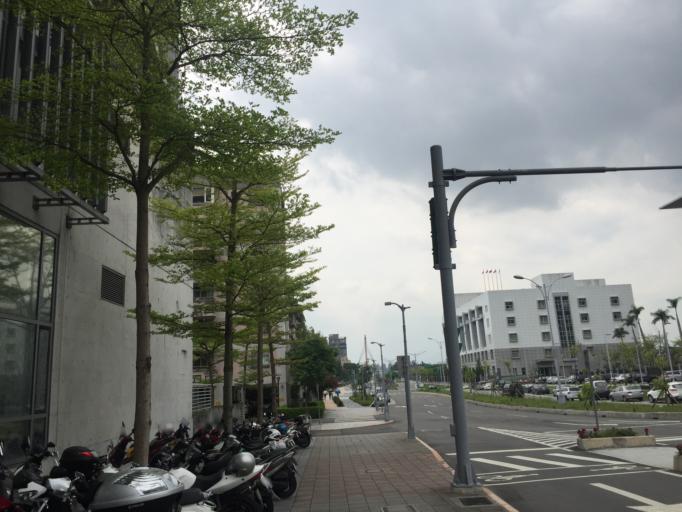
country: TW
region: Taipei
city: Taipei
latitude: 25.0845
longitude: 121.5446
